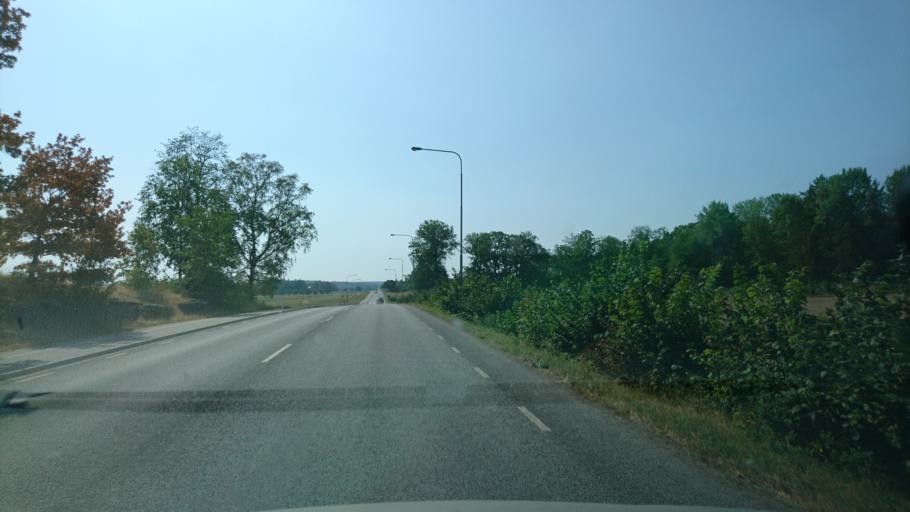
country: SE
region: Uppsala
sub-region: Uppsala Kommun
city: Uppsala
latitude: 59.8252
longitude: 17.6452
